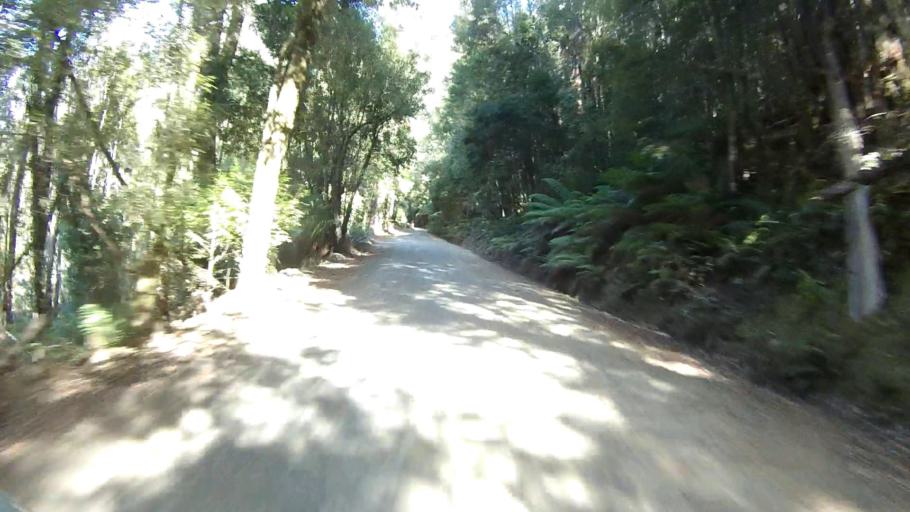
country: AU
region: Tasmania
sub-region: Derwent Valley
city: New Norfolk
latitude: -42.6778
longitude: 146.6909
